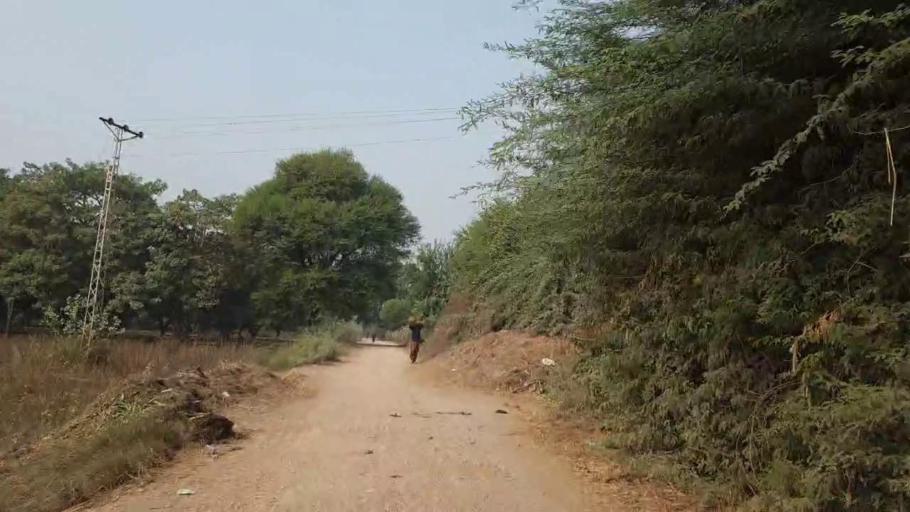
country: PK
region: Sindh
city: Tando Muhammad Khan
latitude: 25.2206
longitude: 68.5527
